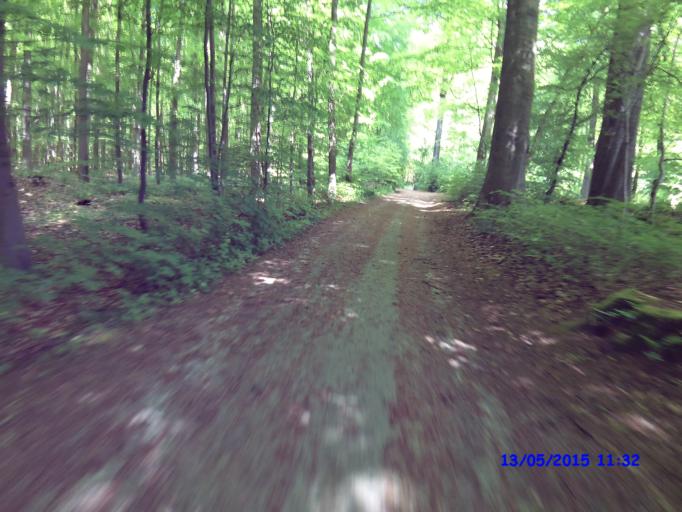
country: BE
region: Flanders
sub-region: Provincie Vlaams-Brabant
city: Hoeilaart
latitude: 50.7683
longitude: 4.4293
